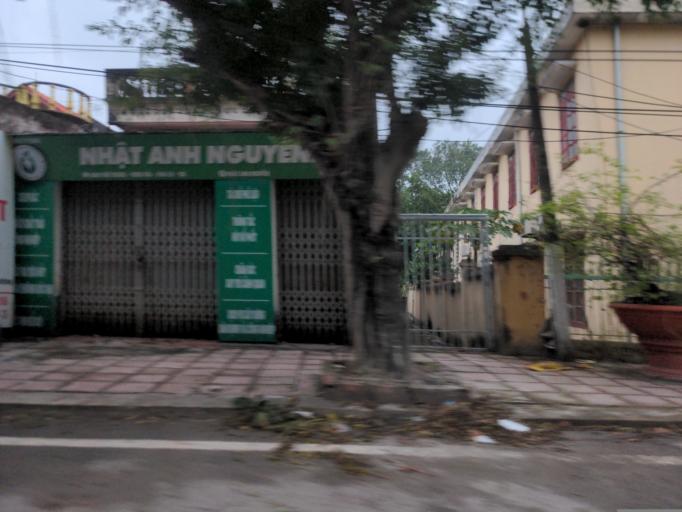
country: VN
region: Ninh Binh
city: Thi Tran Tam Diep
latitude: 20.2156
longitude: 105.9329
